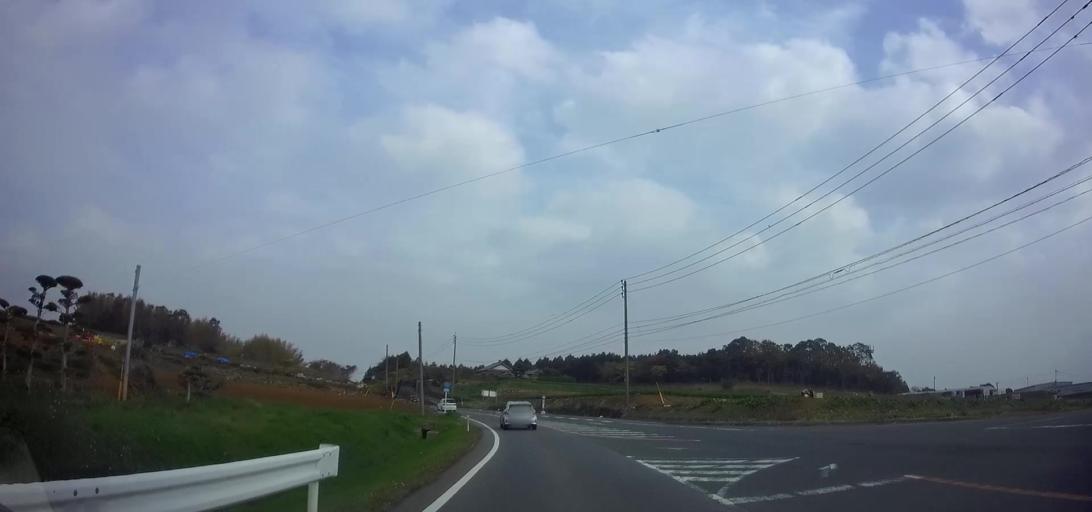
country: JP
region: Nagasaki
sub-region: Isahaya-shi
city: Isahaya
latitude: 32.7860
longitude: 130.0457
